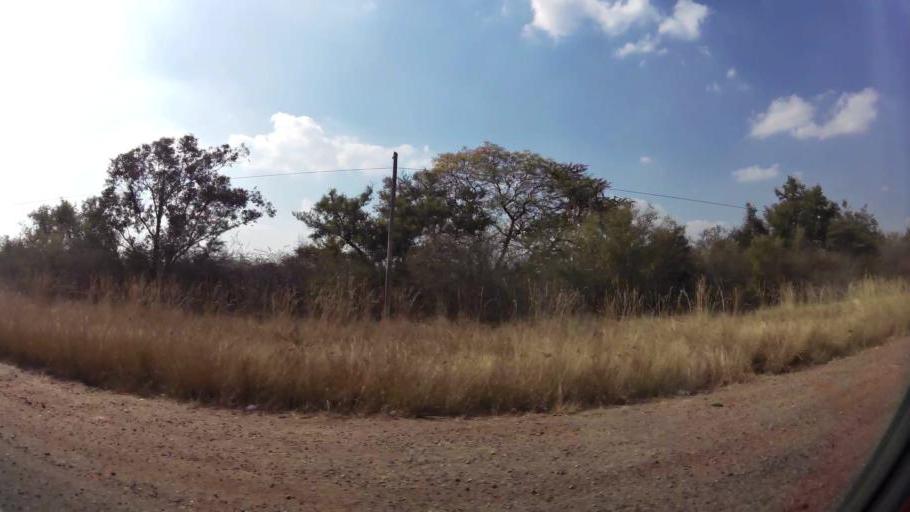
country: ZA
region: North-West
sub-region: Bojanala Platinum District Municipality
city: Rustenburg
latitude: -25.5215
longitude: 27.1062
